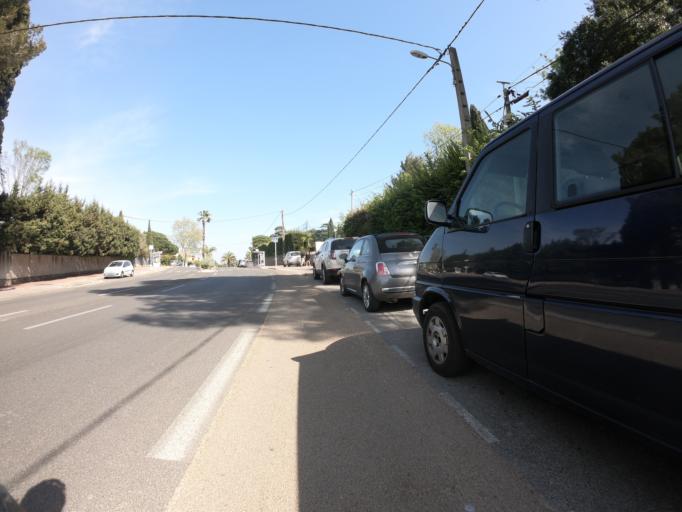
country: FR
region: Provence-Alpes-Cote d'Azur
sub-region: Departement du Var
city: La Valette-du-Var
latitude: 43.1100
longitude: 5.9761
